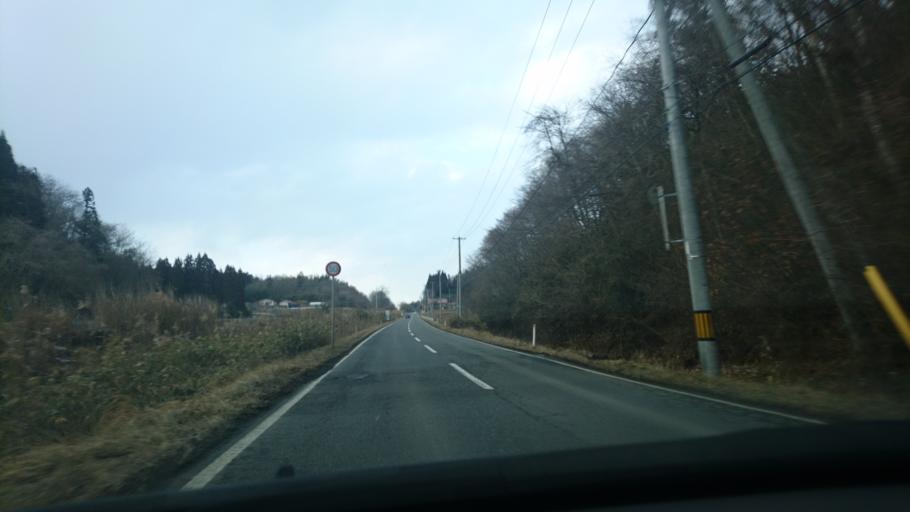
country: JP
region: Iwate
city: Ichinoseki
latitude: 38.9636
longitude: 141.3343
